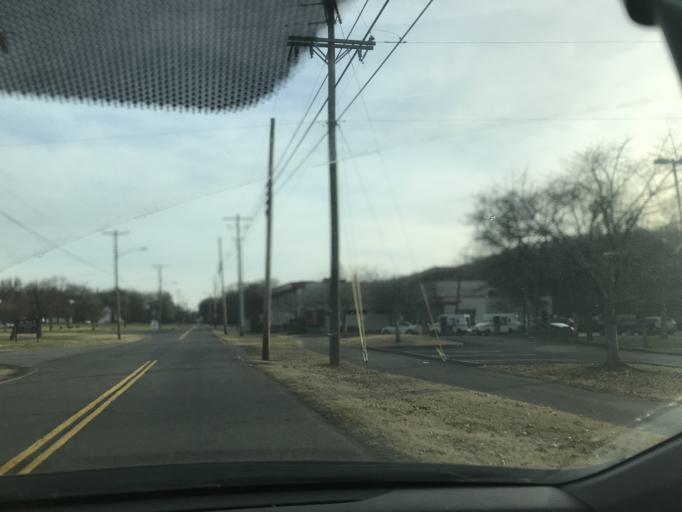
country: US
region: Tennessee
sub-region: Davidson County
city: Nashville
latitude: 36.2105
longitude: -86.8239
